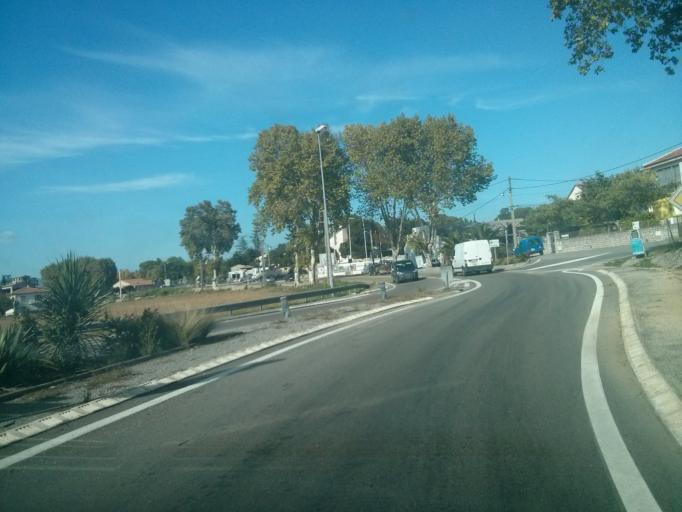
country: FR
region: Languedoc-Roussillon
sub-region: Departement du Gard
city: Quissac
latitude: 43.9061
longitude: 4.0049
